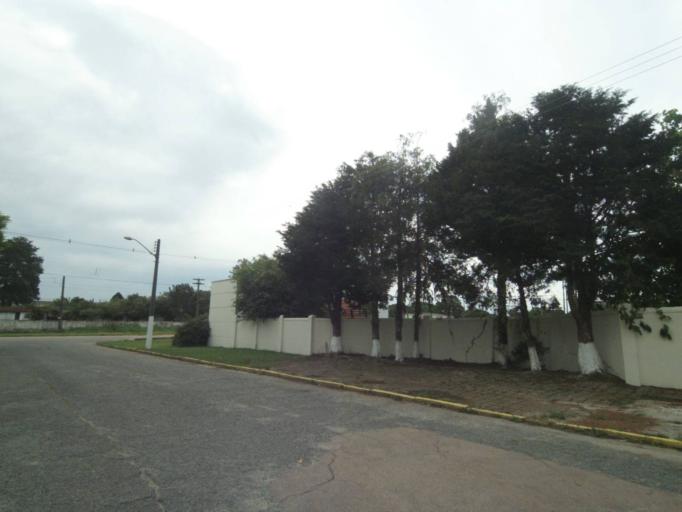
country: BR
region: Parana
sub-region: Pinhais
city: Pinhais
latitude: -25.4275
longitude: -49.2215
